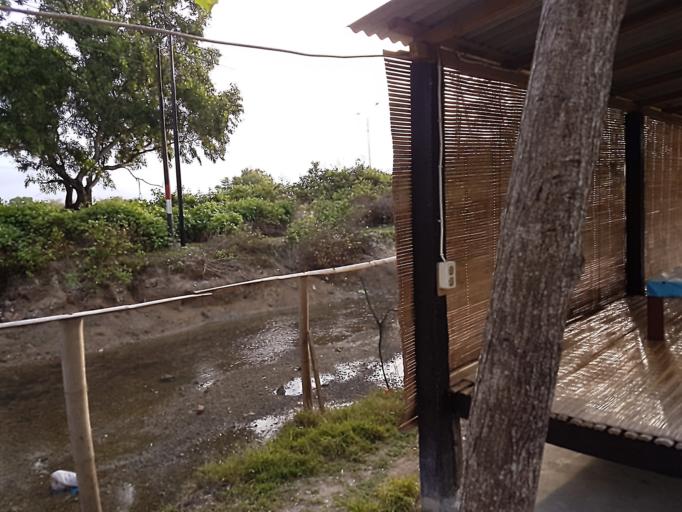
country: ID
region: Bali
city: Karyadharma
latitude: -8.7282
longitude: 115.2303
